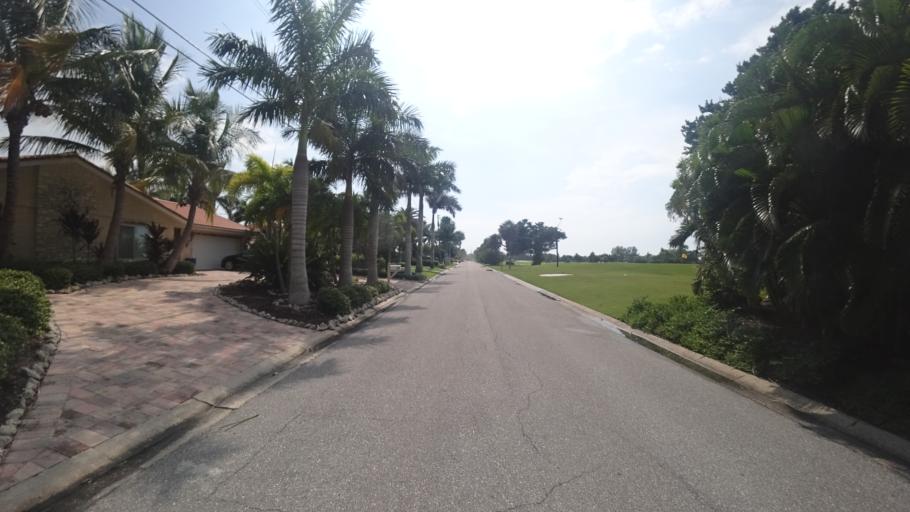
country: US
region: Florida
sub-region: Manatee County
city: Anna Maria
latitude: 27.5246
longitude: -82.7138
